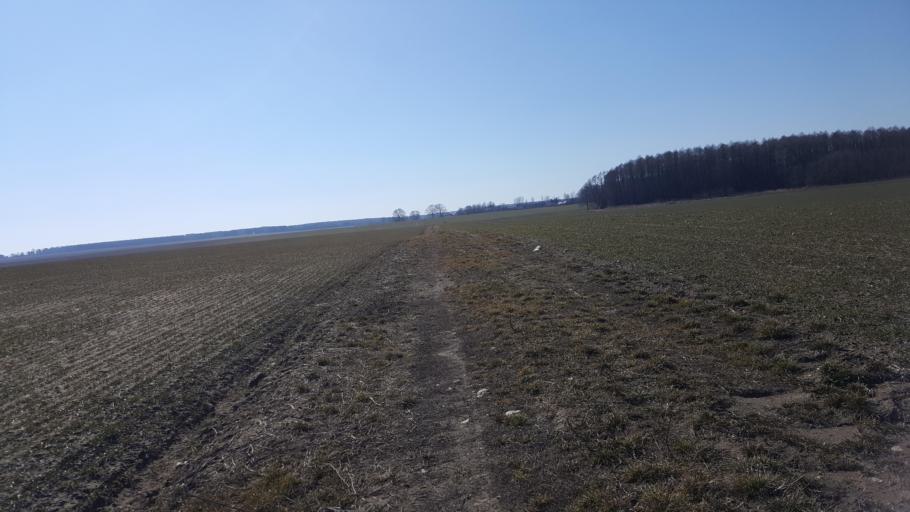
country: BY
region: Brest
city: Kamyanyets
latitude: 52.3686
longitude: 23.7742
